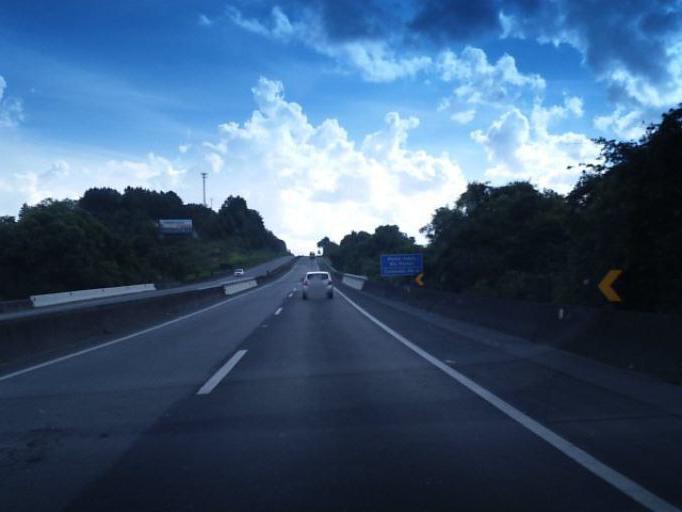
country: BR
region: Parana
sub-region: Campina Grande Do Sul
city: Campina Grande do Sul
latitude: -25.3329
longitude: -49.0330
